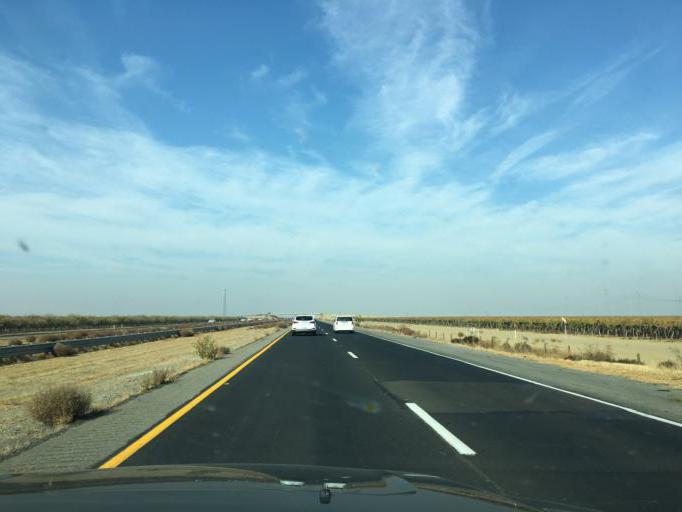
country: US
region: California
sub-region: Kings County
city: Kettleman City
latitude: 35.8695
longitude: -119.8467
